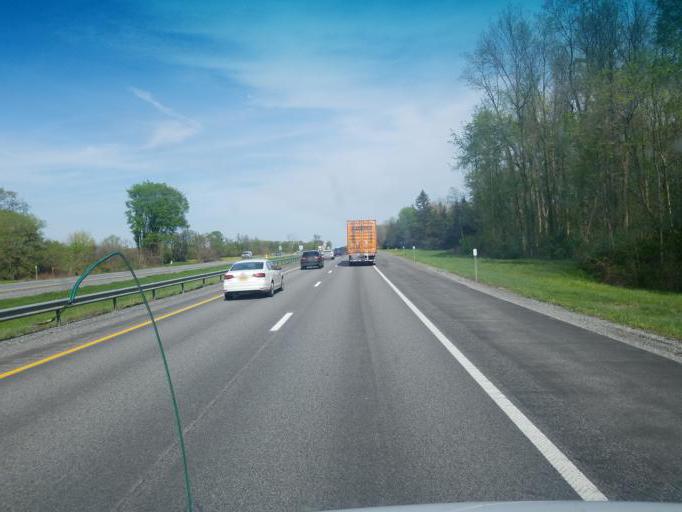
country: US
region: New York
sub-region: Onondaga County
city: Minoa
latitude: 43.0931
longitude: -75.9720
